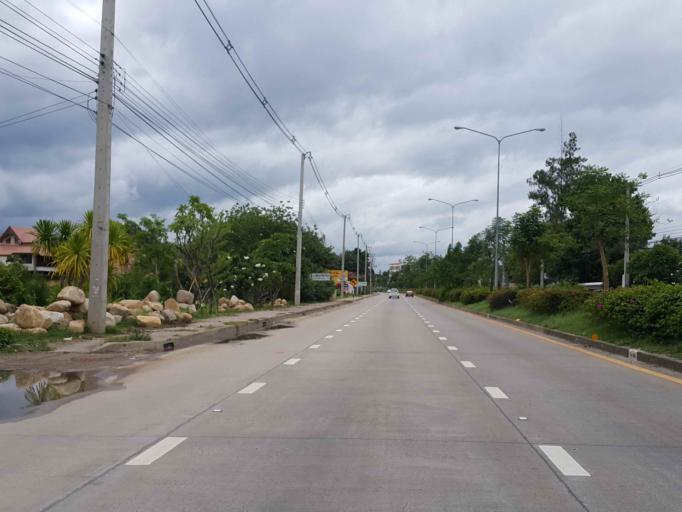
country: TH
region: Chiang Mai
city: San Sai
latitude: 18.8431
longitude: 98.9963
